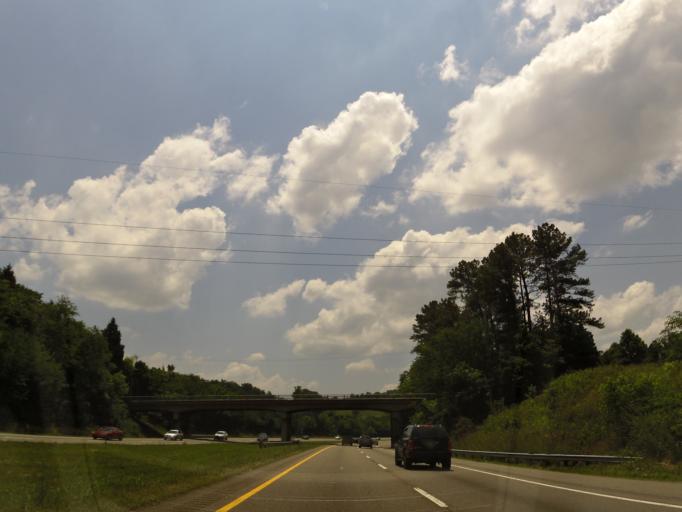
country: US
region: Tennessee
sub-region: Loudon County
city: Lenoir City
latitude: 35.8630
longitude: -84.2586
